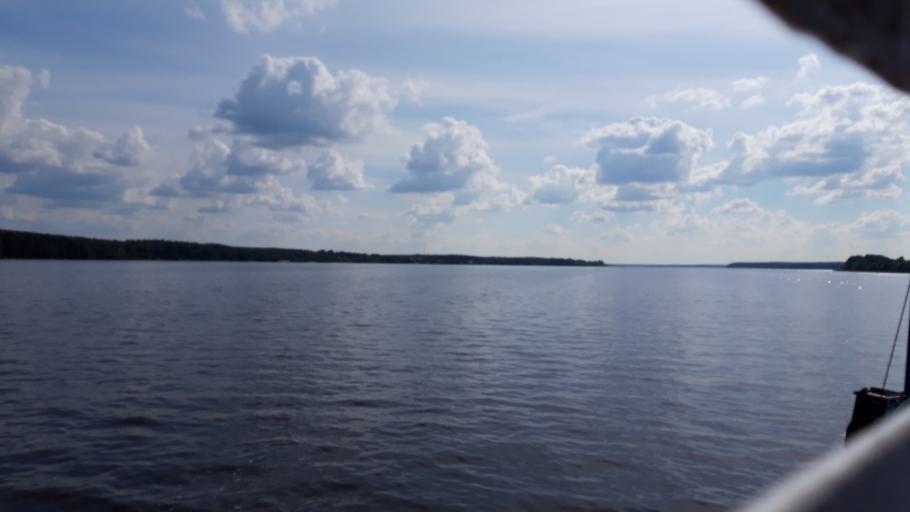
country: RU
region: Tverskaya
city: Konakovo
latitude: 56.6815
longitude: 36.6831
